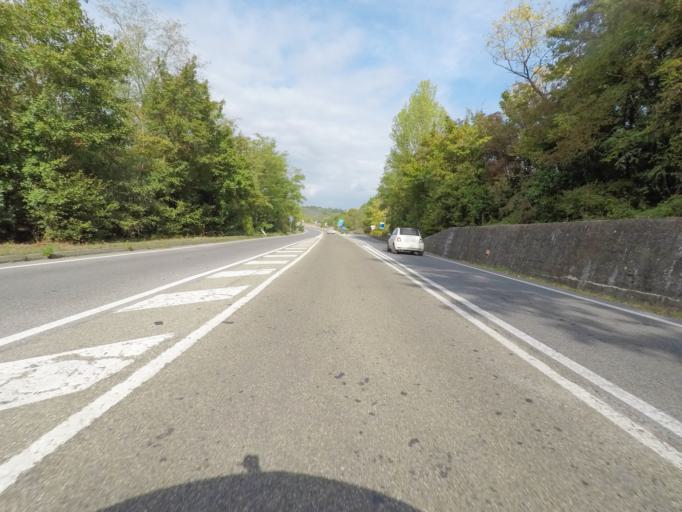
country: IT
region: Tuscany
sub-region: Provincia di Siena
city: Belverde
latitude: 43.3542
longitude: 11.3056
